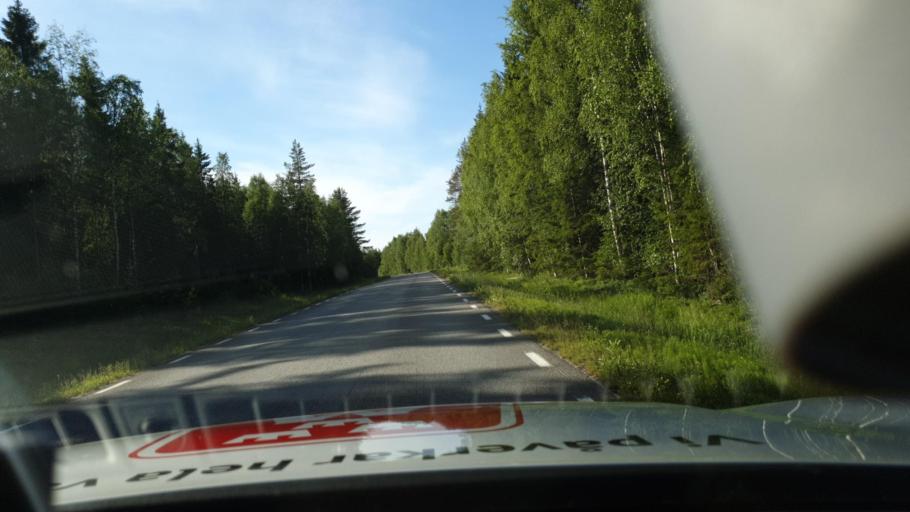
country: SE
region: Norrbotten
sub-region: Kalix Kommun
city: Toere
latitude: 65.8878
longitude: 22.6530
